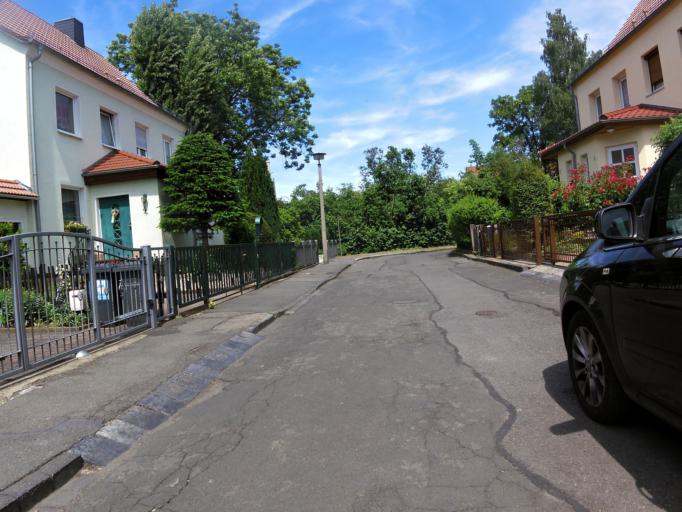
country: DE
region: Saxony
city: Markkleeberg
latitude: 51.3023
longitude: 12.3906
